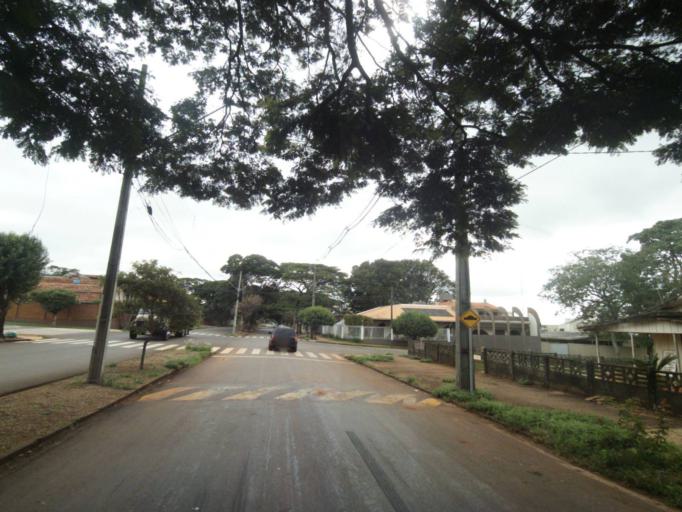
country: BR
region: Parana
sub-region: Campo Mourao
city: Campo Mourao
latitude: -24.0455
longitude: -52.3722
